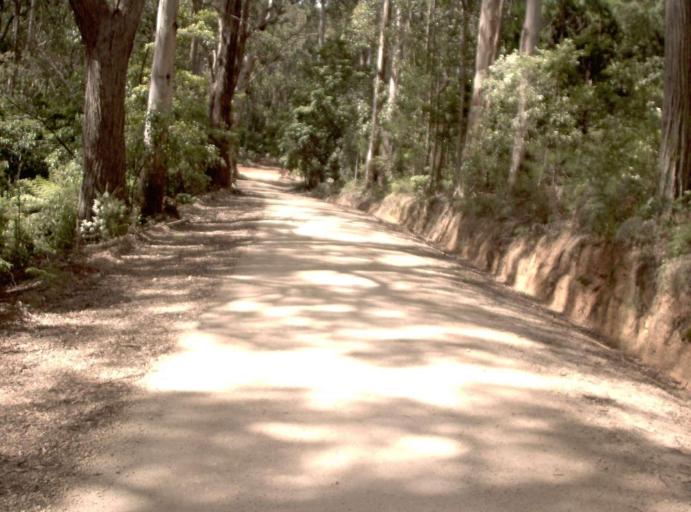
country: AU
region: Victoria
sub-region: East Gippsland
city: Lakes Entrance
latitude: -37.5840
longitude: 148.7263
